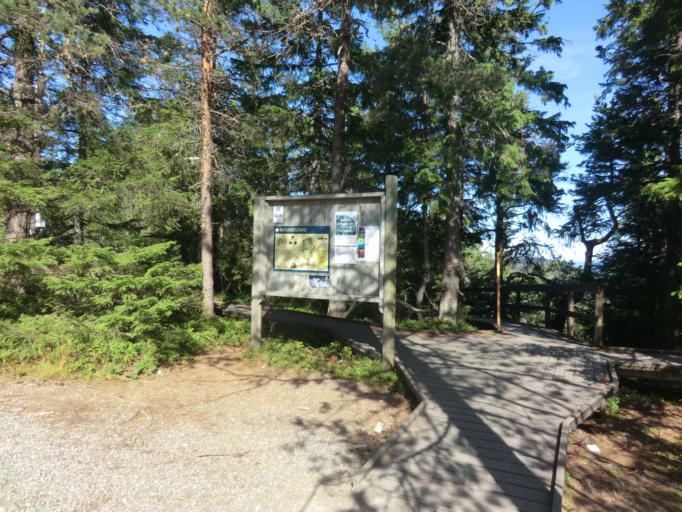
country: SE
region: Vaesternorrland
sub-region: Kramfors Kommun
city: Nordingra
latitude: 63.0757
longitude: 18.3498
